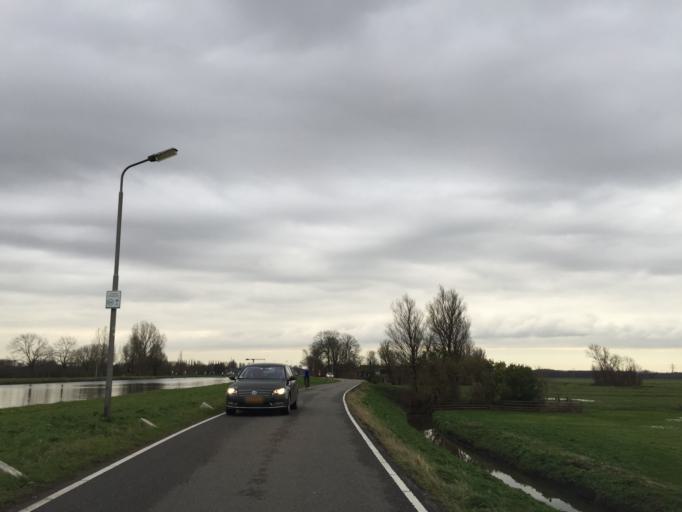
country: NL
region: South Holland
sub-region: Gemeente Schiedam
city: Schiedam
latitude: 51.9679
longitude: 4.3892
